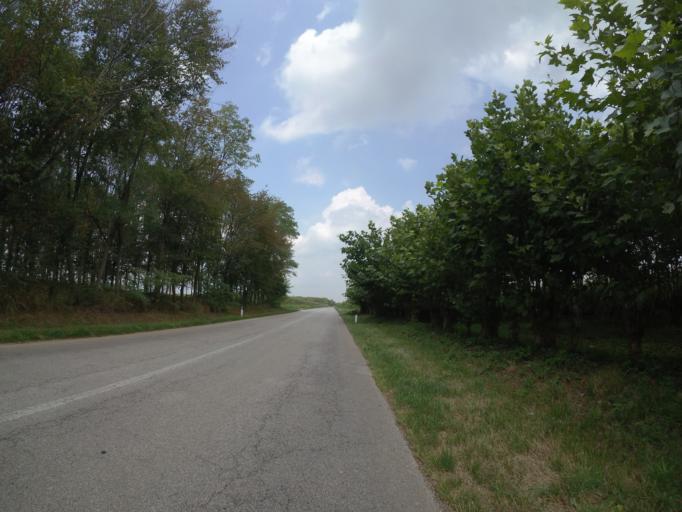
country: IT
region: Friuli Venezia Giulia
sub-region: Provincia di Udine
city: Sedegliano
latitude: 46.0124
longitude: 13.0071
